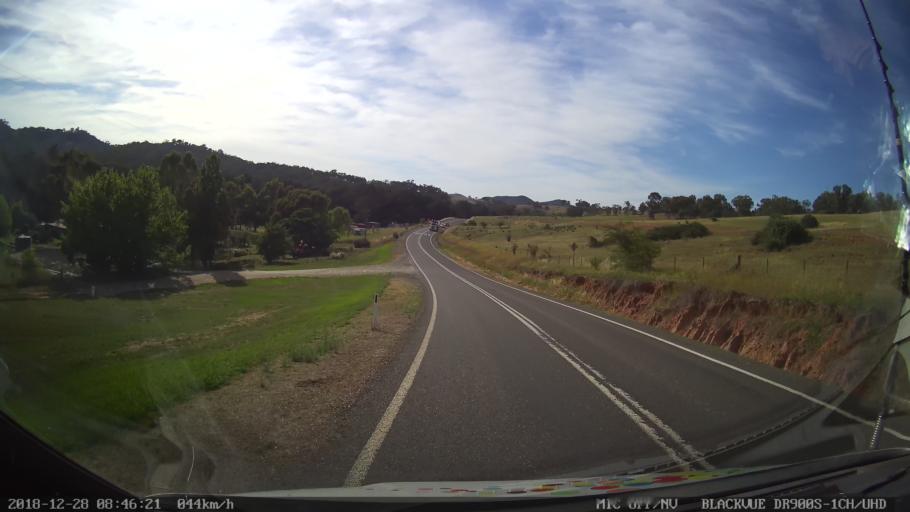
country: AU
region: New South Wales
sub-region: Upper Lachlan Shire
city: Crookwell
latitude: -34.0188
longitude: 149.3302
